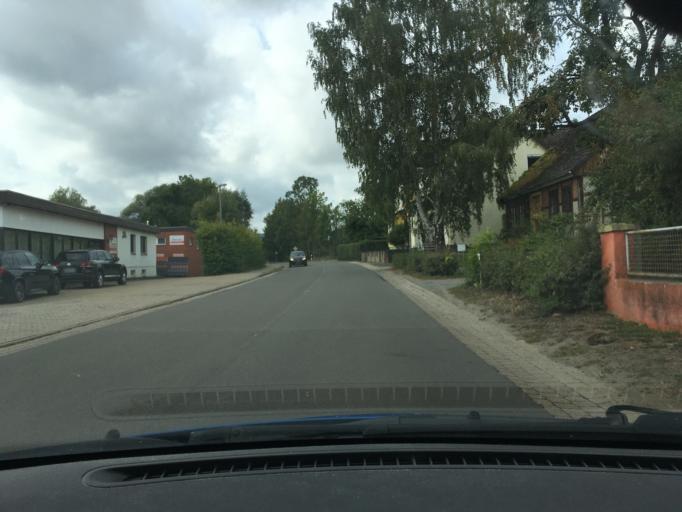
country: DE
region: Lower Saxony
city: Bad Munder am Deister
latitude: 52.1981
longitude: 9.4390
